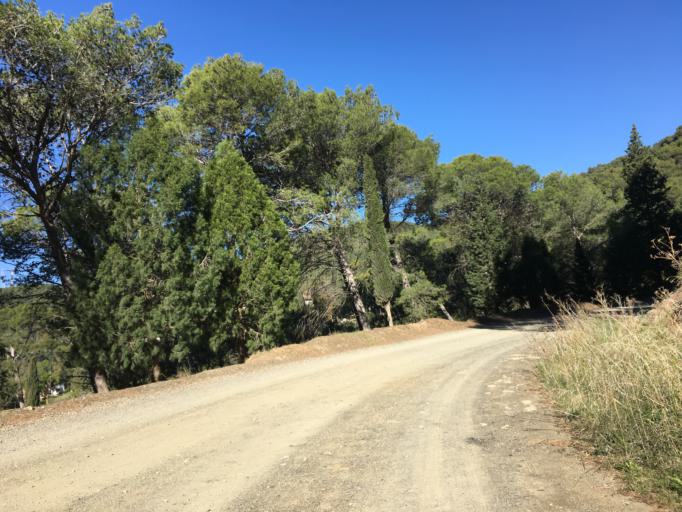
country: ES
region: Andalusia
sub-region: Provincia de Malaga
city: Malaga
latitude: 36.7758
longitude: -4.3848
